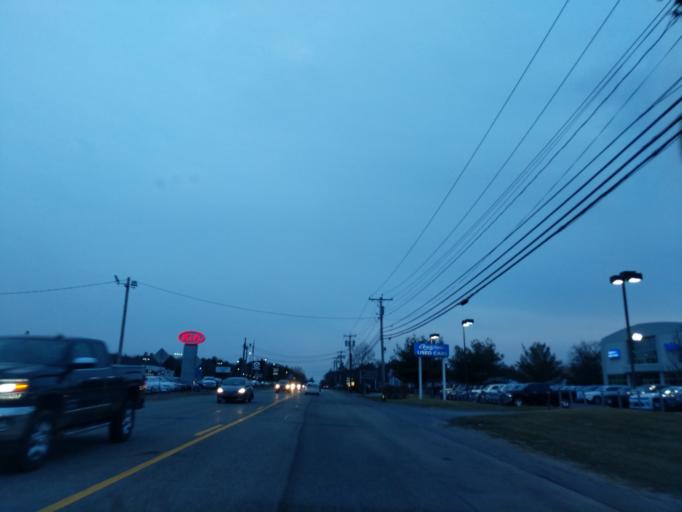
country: US
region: Massachusetts
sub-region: Bristol County
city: Raynham Center
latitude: 41.9038
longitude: -71.0079
